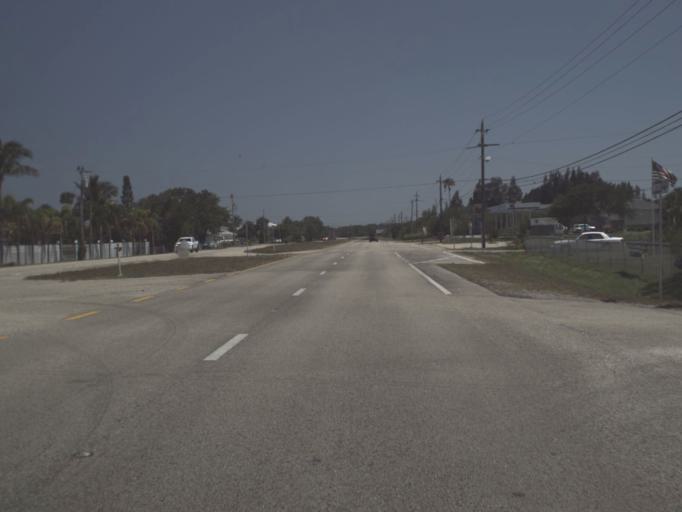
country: US
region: Florida
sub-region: Brevard County
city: Micco
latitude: 27.9190
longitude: -80.5199
